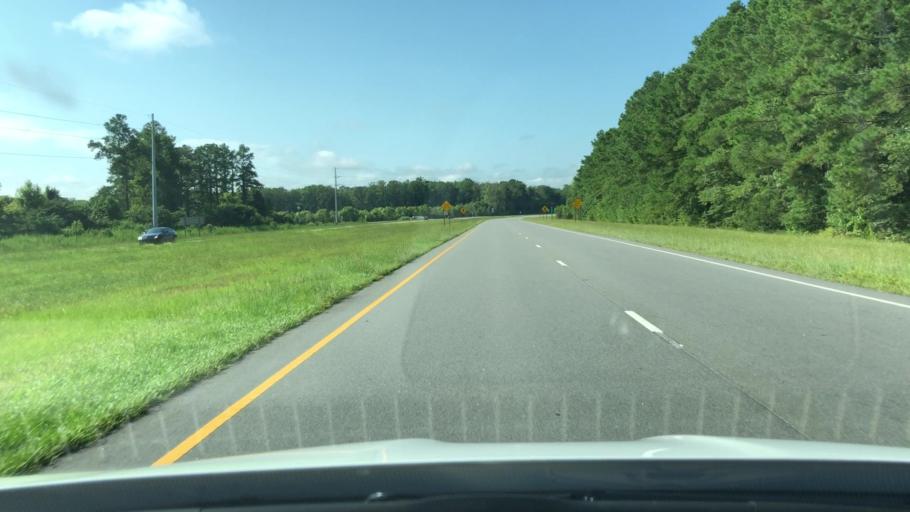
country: US
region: North Carolina
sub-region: Pasquotank County
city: Elizabeth City
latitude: 36.4391
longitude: -76.3389
